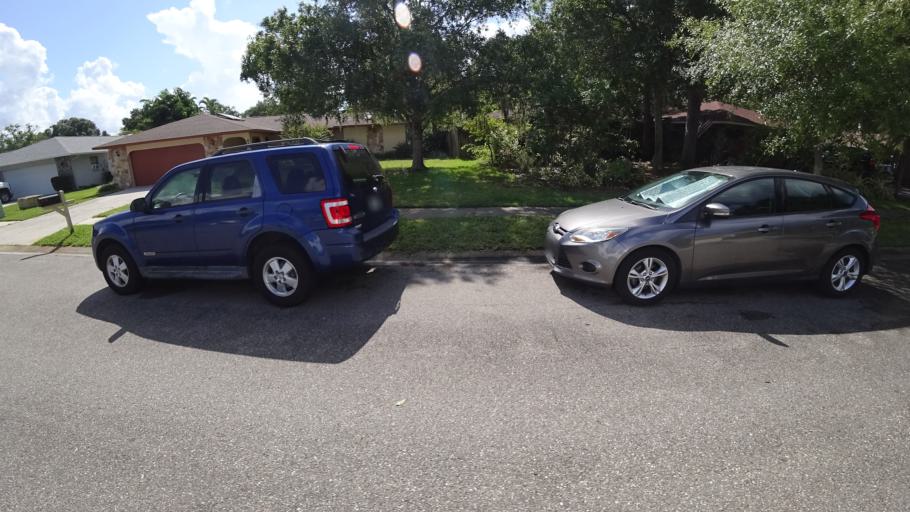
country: US
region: Florida
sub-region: Sarasota County
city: Desoto Lakes
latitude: 27.3896
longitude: -82.4994
